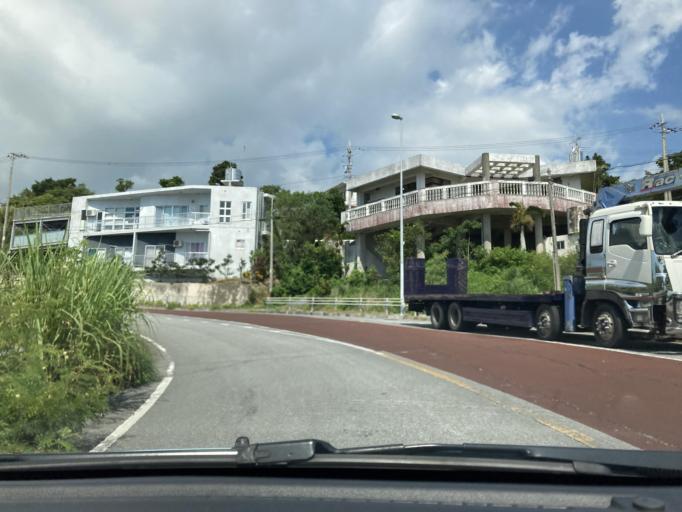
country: JP
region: Okinawa
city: Tomigusuku
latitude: 26.1416
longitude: 127.7707
